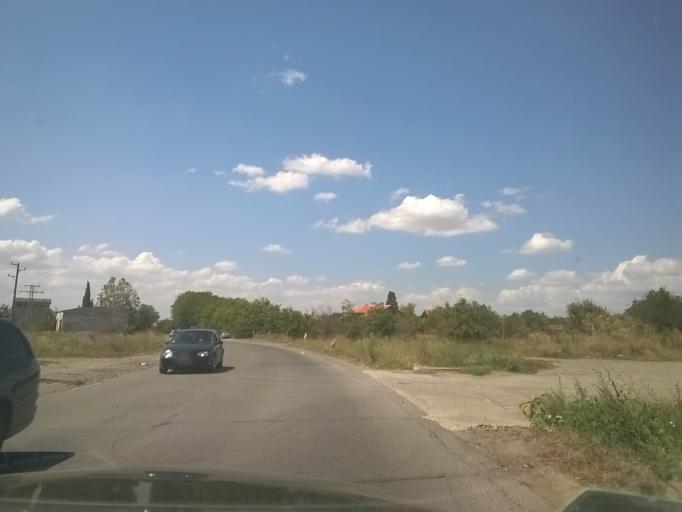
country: BG
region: Burgas
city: Aheloy
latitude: 42.6566
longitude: 27.5757
